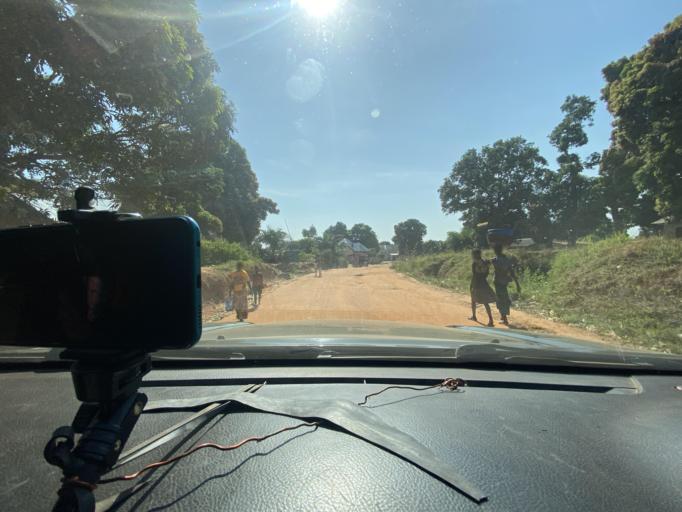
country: CD
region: Kasai-Oriental
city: Kabinda
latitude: -6.1277
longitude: 24.4985
